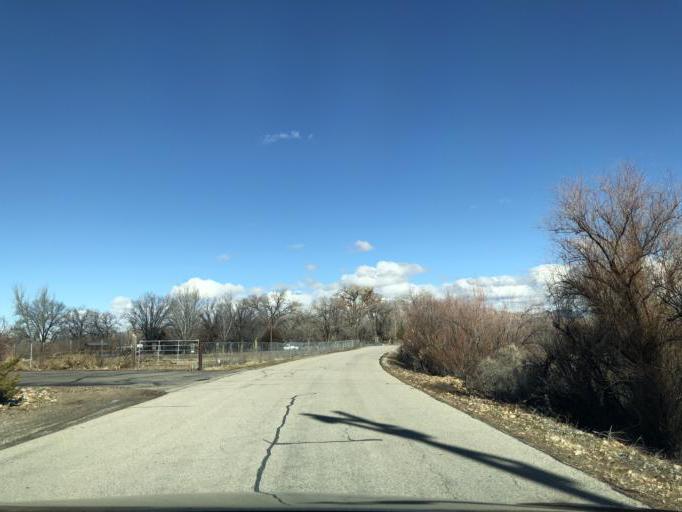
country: US
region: Utah
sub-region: Carbon County
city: East Carbon City
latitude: 39.0006
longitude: -110.1569
